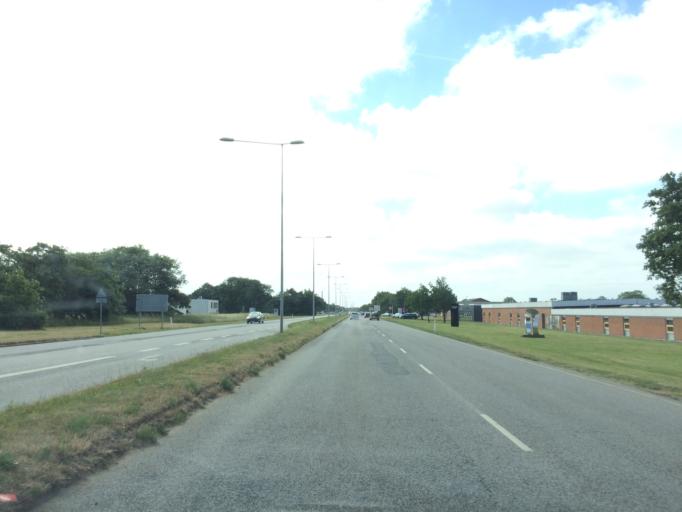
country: DK
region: Central Jutland
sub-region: Herning Kommune
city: Snejbjerg
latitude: 56.1608
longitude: 8.9247
